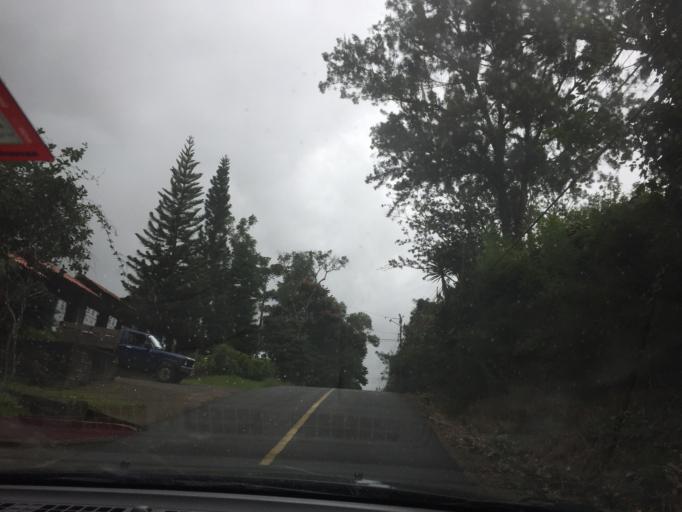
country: CR
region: Heredia
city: Angeles
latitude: 10.0131
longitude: -84.0334
